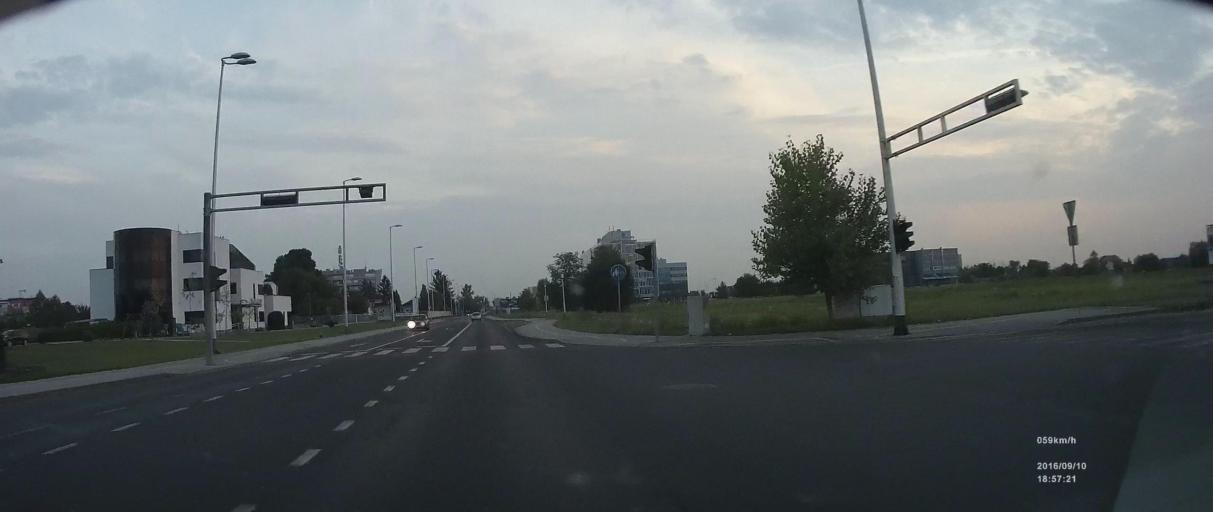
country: HR
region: Grad Zagreb
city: Novi Zagreb
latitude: 45.7674
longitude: 15.9806
